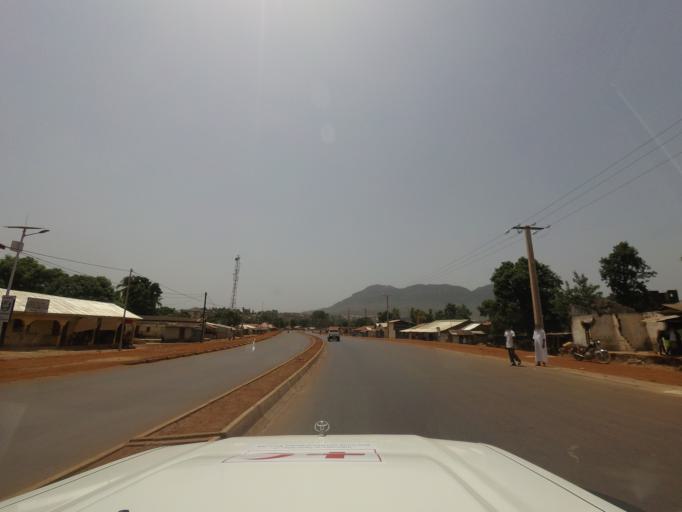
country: GN
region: Kindia
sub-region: Coyah
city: Coyah
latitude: 9.7222
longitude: -13.4139
